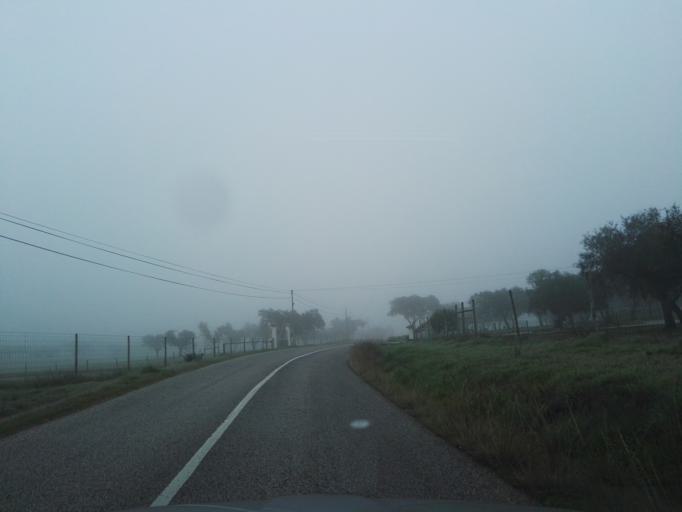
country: PT
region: Evora
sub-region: Montemor-O-Novo
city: Montemor-o-Novo
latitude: 38.7698
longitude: -8.1970
